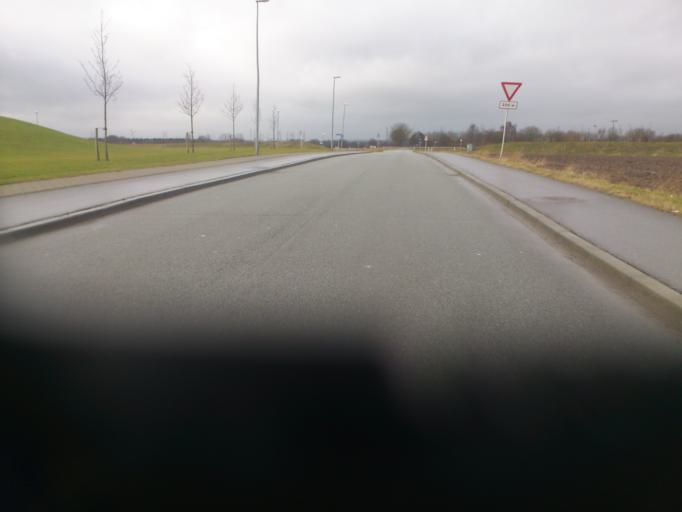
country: DK
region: South Denmark
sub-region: Fredericia Kommune
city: Fredericia
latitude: 55.5824
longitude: 9.7012
